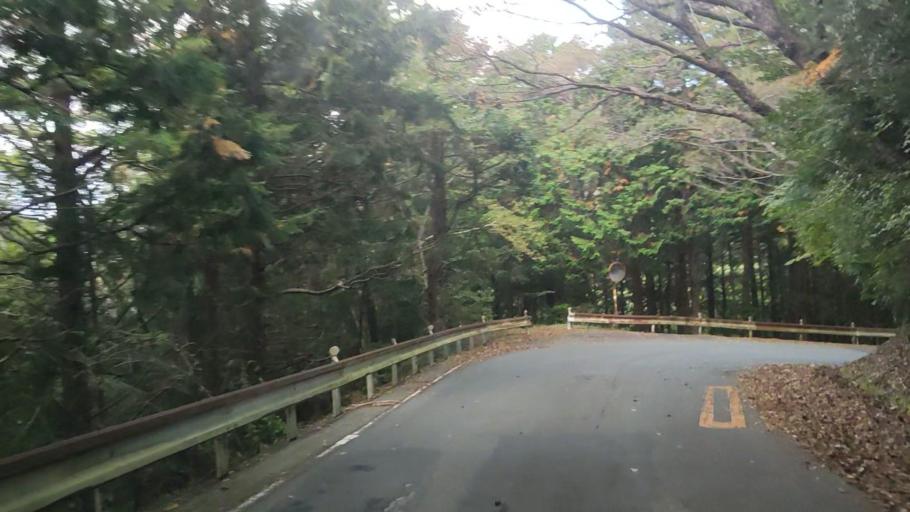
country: JP
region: Shizuoka
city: Ito
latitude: 34.9541
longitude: 139.0512
